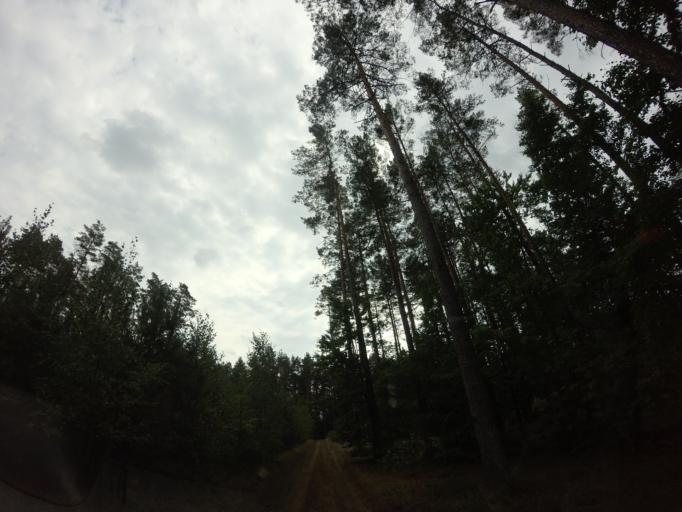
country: PL
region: West Pomeranian Voivodeship
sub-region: Powiat drawski
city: Drawsko Pomorskie
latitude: 53.4590
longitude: 15.7214
